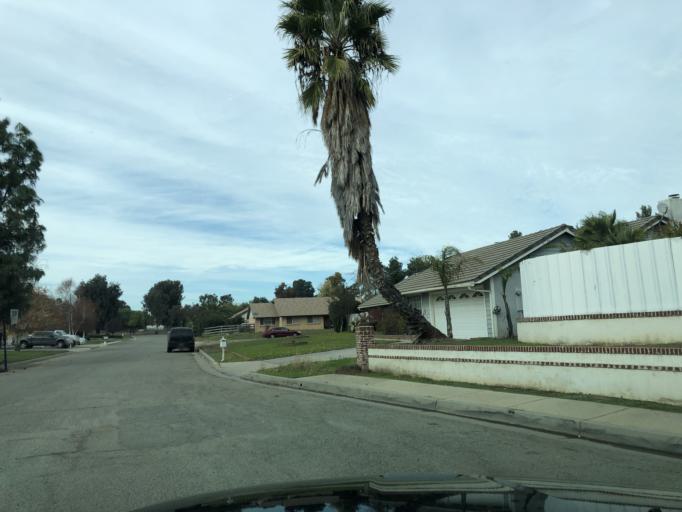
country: US
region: California
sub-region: Riverside County
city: Wildomar
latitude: 33.6103
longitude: -117.2705
